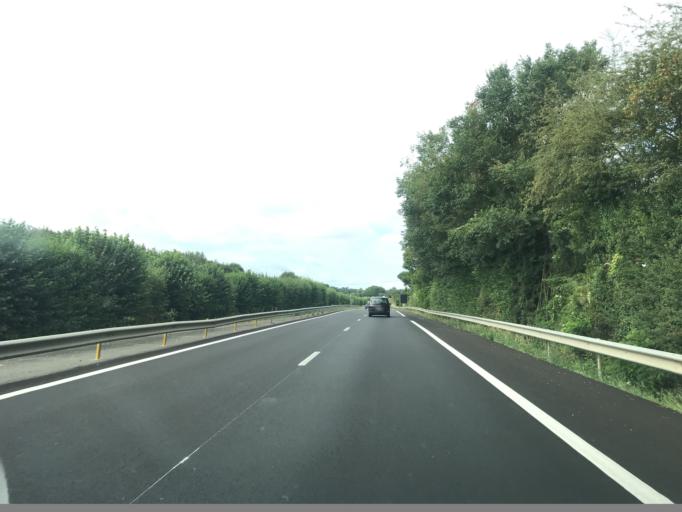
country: FR
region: Poitou-Charentes
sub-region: Departement de la Vienne
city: Couhe
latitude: 46.3567
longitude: 0.1937
